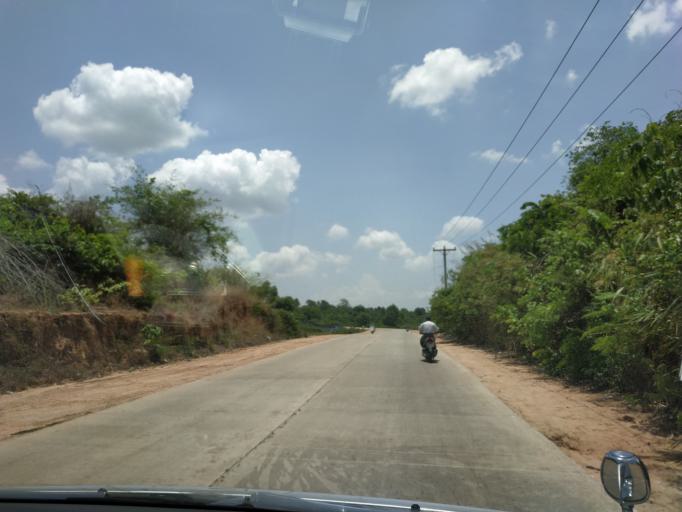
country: MM
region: Bago
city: Bago
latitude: 17.4672
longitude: 96.4616
